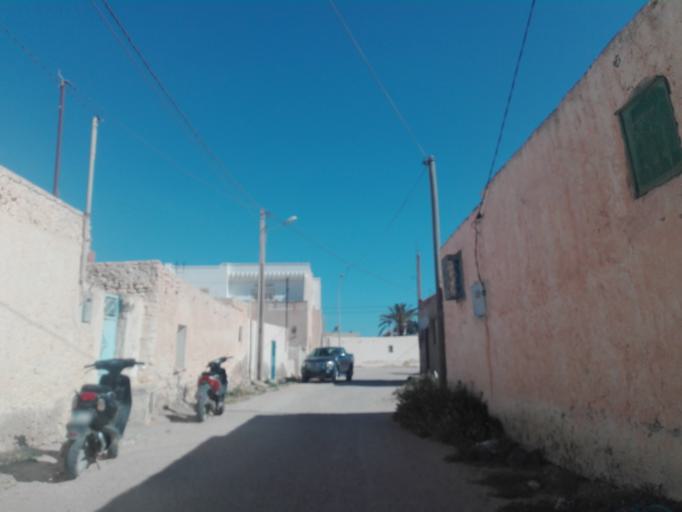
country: TN
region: Safaqis
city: Al Qarmadah
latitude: 34.7119
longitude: 11.2021
